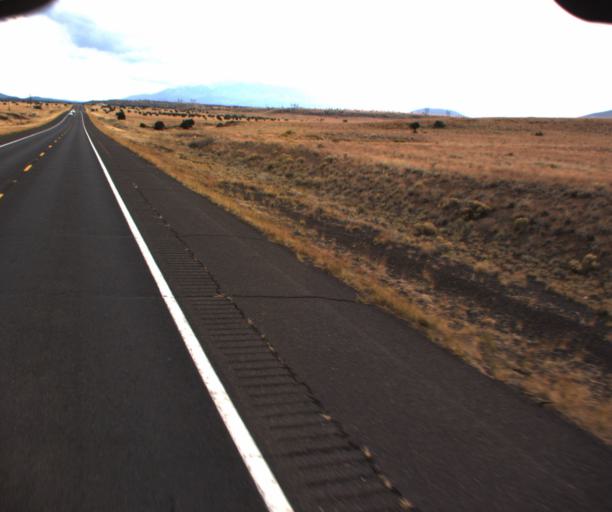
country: US
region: Arizona
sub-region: Coconino County
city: Flagstaff
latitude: 35.5550
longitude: -111.5357
